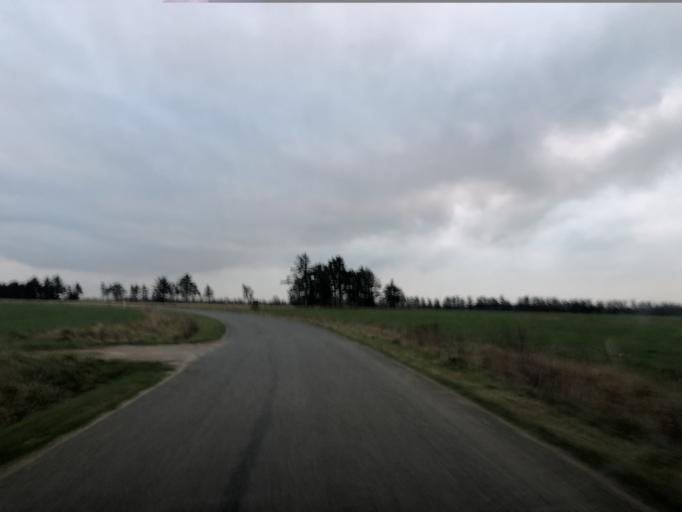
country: DK
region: Central Jutland
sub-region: Holstebro Kommune
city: Ulfborg
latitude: 56.2472
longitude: 8.2808
